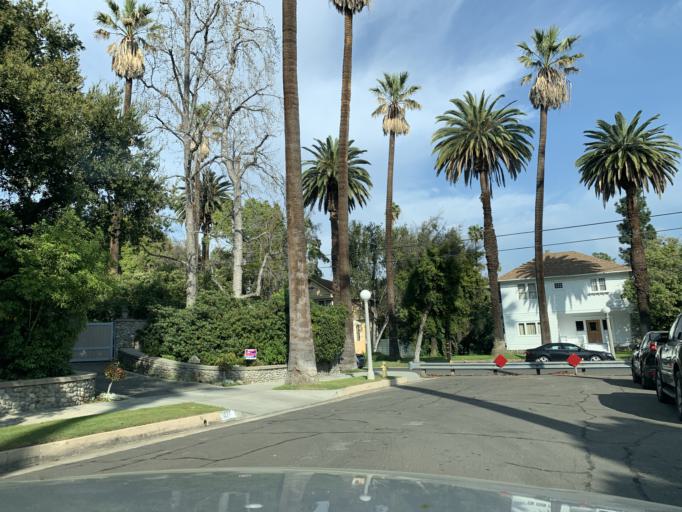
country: US
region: California
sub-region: Los Angeles County
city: South Pasadena
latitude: 34.1329
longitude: -118.1559
